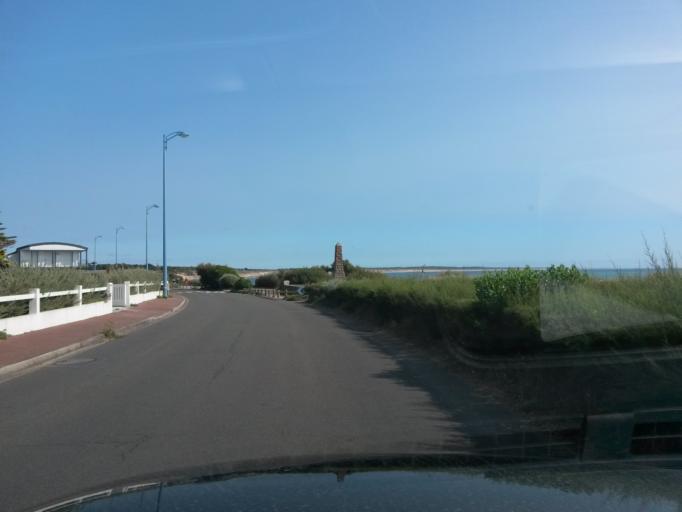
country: FR
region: Pays de la Loire
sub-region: Departement de la Vendee
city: Bretignolles-sur-Mer
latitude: 46.6170
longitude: -1.8695
